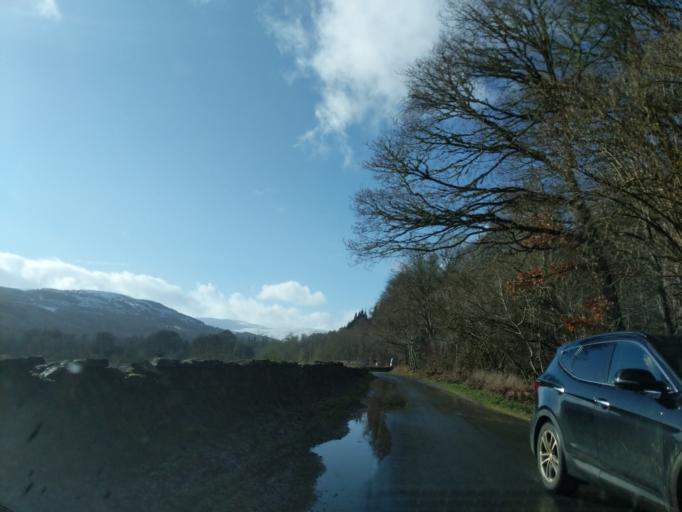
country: GB
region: Scotland
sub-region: Perth and Kinross
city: Aberfeldy
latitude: 56.6061
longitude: -3.9750
